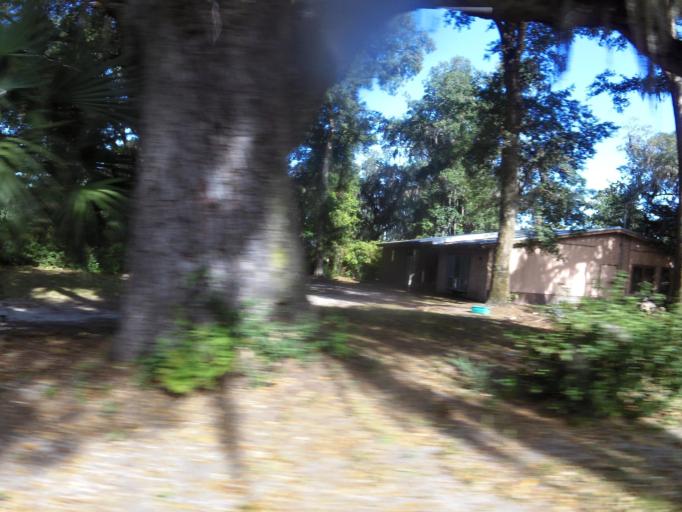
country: US
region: Georgia
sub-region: Glynn County
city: Brunswick
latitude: 31.1400
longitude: -81.5582
